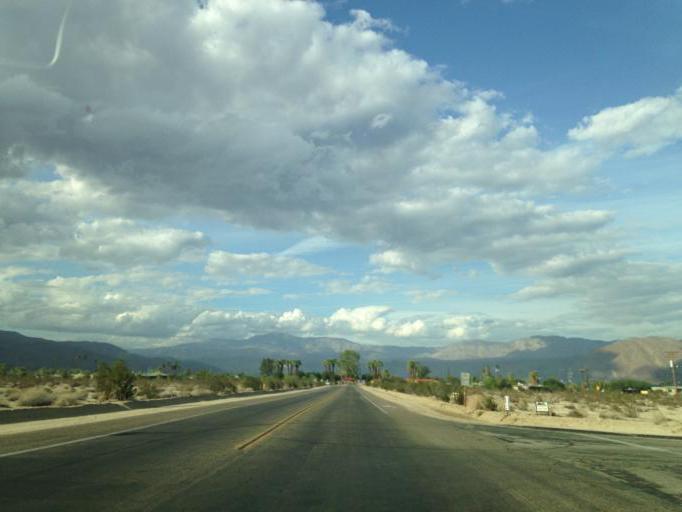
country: US
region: California
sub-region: San Diego County
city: Borrego Springs
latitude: 33.2527
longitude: -116.3747
